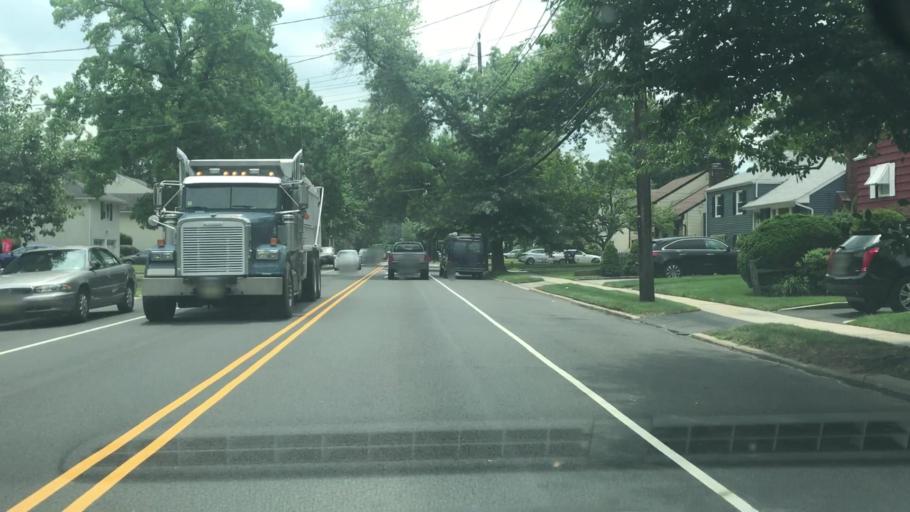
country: US
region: New Jersey
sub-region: Union County
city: Clark
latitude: 40.6442
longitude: -74.3050
